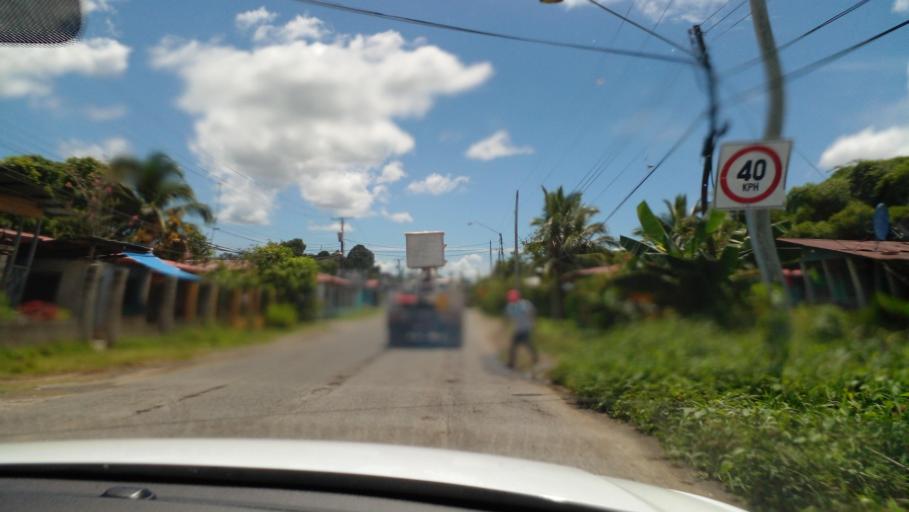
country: PA
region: Bocas del Toro
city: Almirante
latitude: 9.2930
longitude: -82.4057
